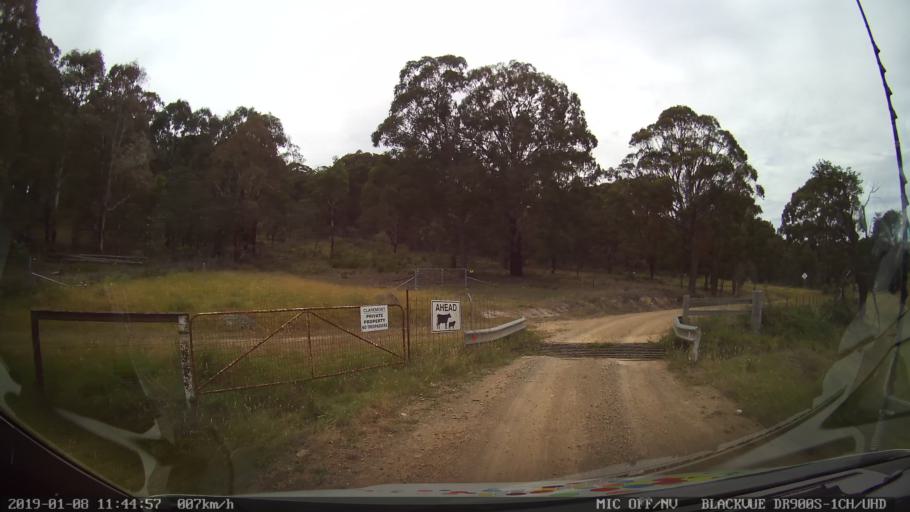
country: AU
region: New South Wales
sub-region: Armidale Dumaresq
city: Armidale
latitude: -30.3803
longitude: 151.5888
